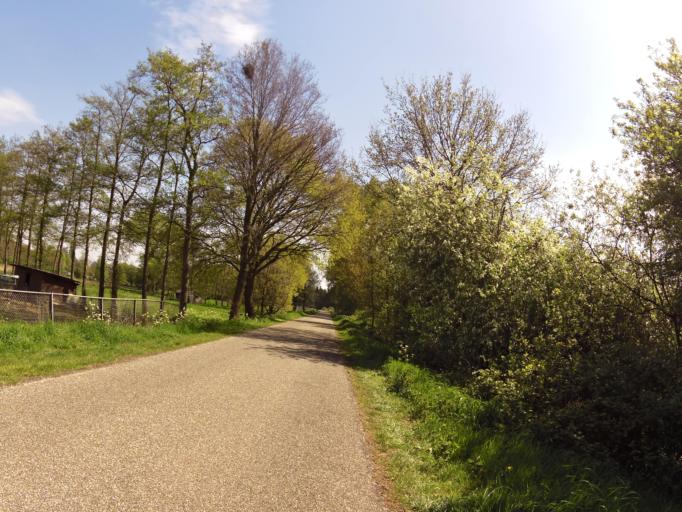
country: NL
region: North Brabant
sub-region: Gemeente Sint-Michielsgestel
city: Sint-Michielsgestel
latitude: 51.6717
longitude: 5.4004
